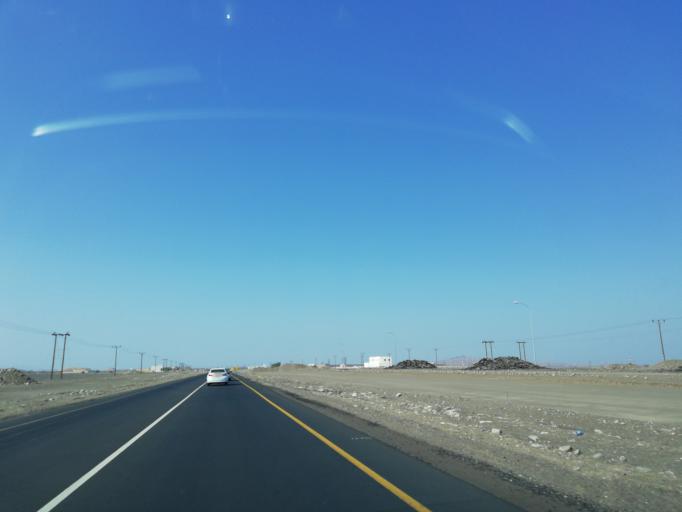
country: OM
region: Ash Sharqiyah
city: Ibra'
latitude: 22.7087
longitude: 58.1432
